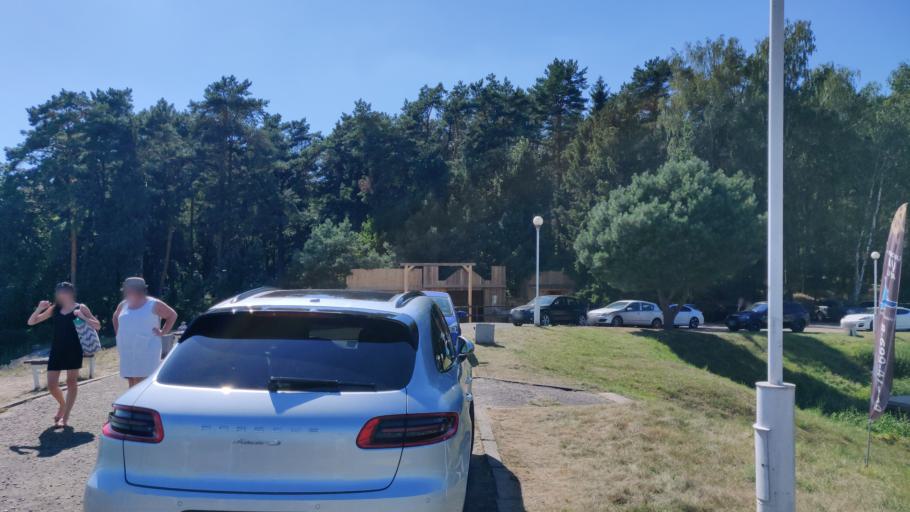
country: LT
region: Kauno apskritis
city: Dainava (Kaunas)
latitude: 54.8840
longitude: 24.0250
